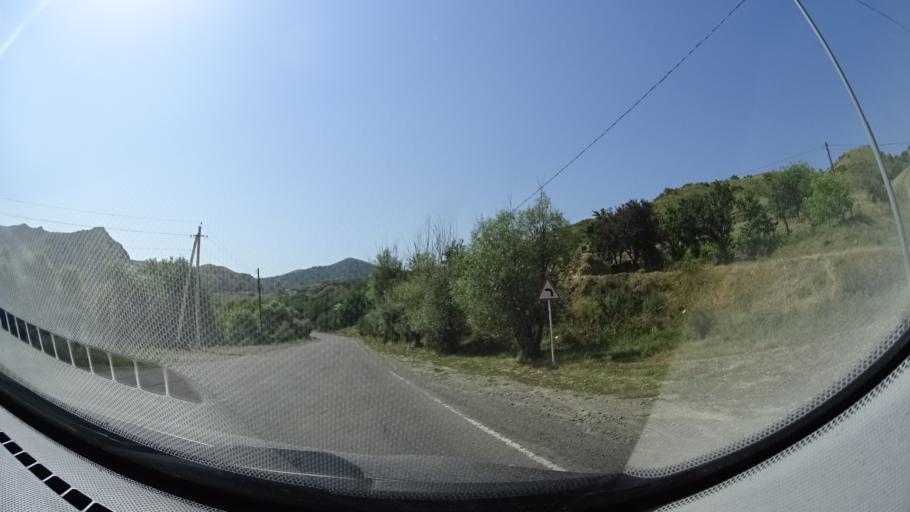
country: GE
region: Samtskhe-Javakheti
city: Akhaltsikhe
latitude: 41.6331
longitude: 43.0436
